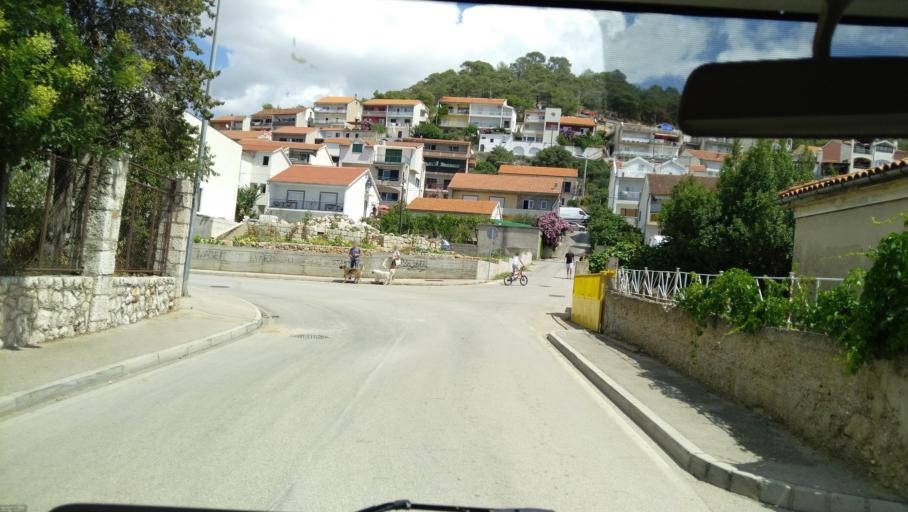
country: HR
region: Sibensko-Kniniska
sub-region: Grad Sibenik
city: Sibenik
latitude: 43.7436
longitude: 15.8870
